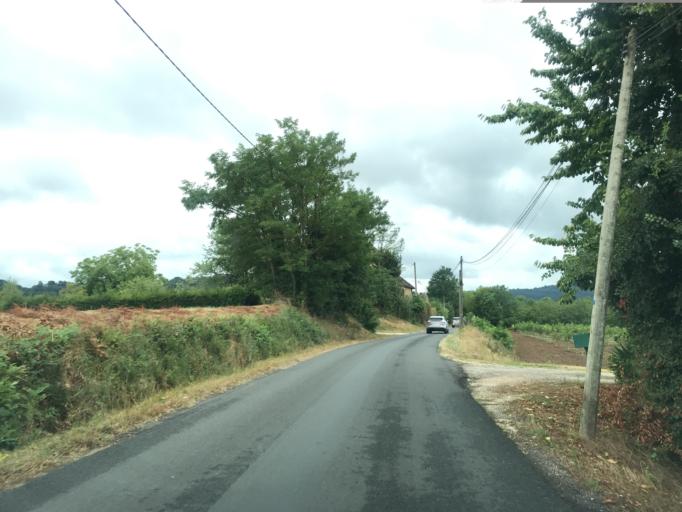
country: FR
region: Aquitaine
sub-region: Departement de la Dordogne
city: Domme
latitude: 44.8184
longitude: 1.2273
